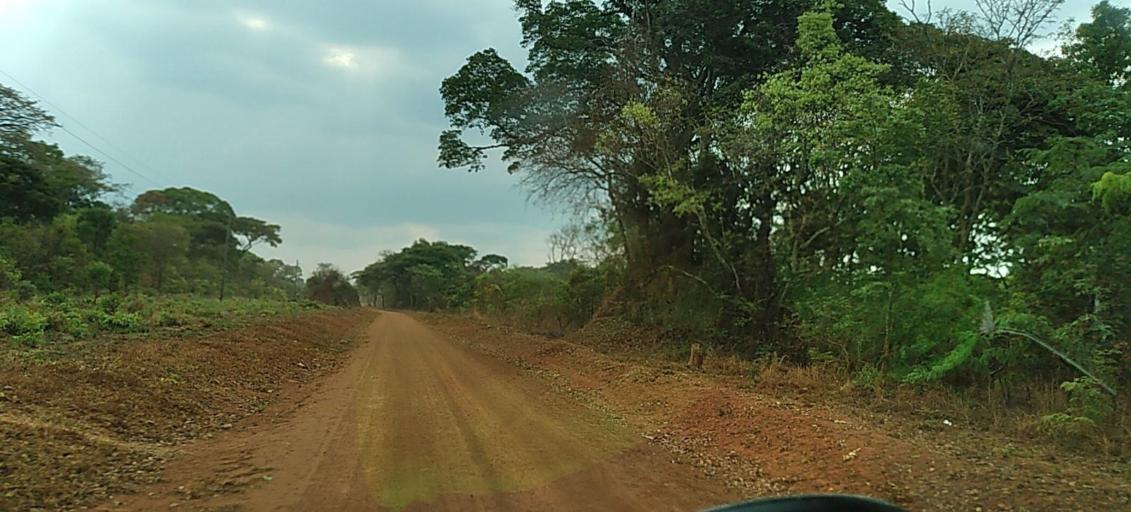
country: ZM
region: North-Western
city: Solwezi
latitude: -12.7845
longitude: 26.5041
